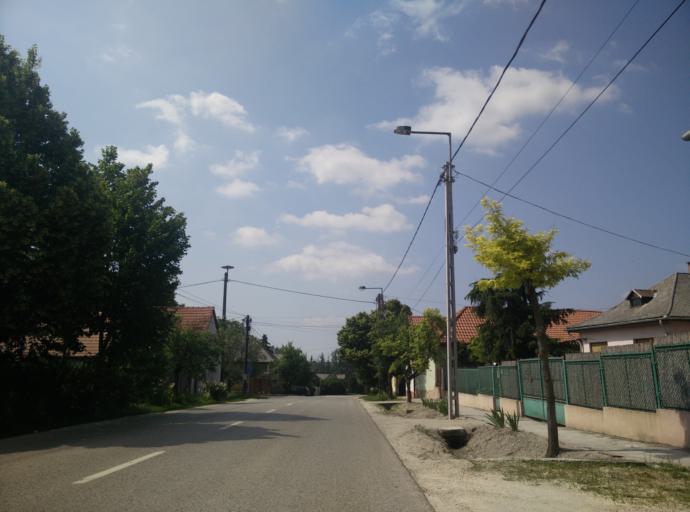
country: HU
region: Pest
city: Biatorbagy
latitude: 47.4661
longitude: 18.8032
